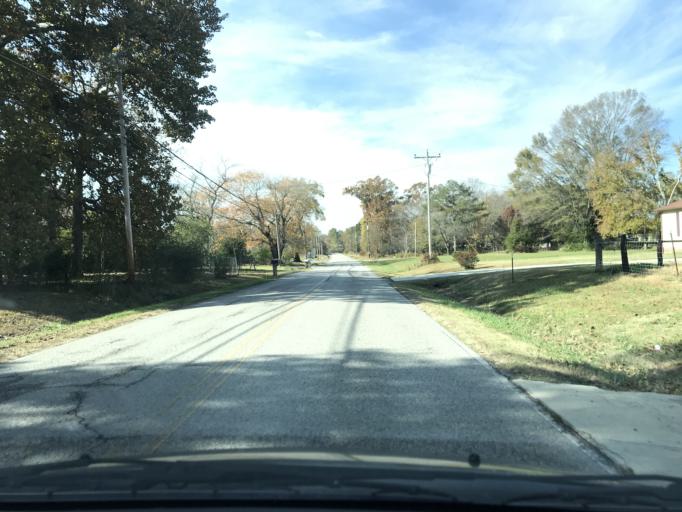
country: US
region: Tennessee
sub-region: Coffee County
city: Tullahoma
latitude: 35.3896
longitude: -86.1628
